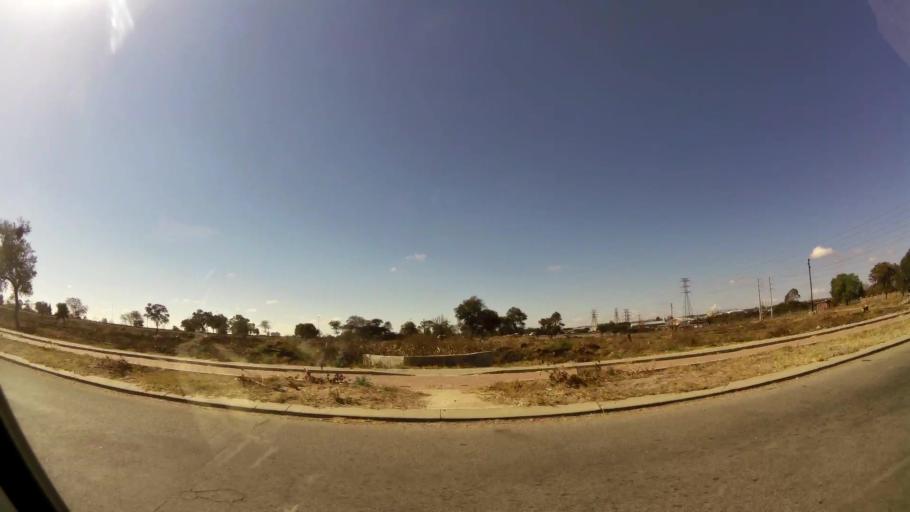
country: ZA
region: Limpopo
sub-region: Capricorn District Municipality
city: Polokwane
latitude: -23.8867
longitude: 29.4254
